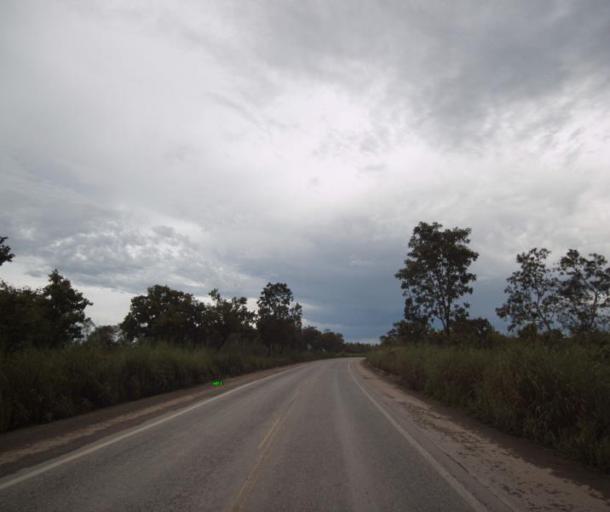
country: BR
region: Goias
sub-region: Porangatu
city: Porangatu
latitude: -13.5565
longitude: -49.0649
